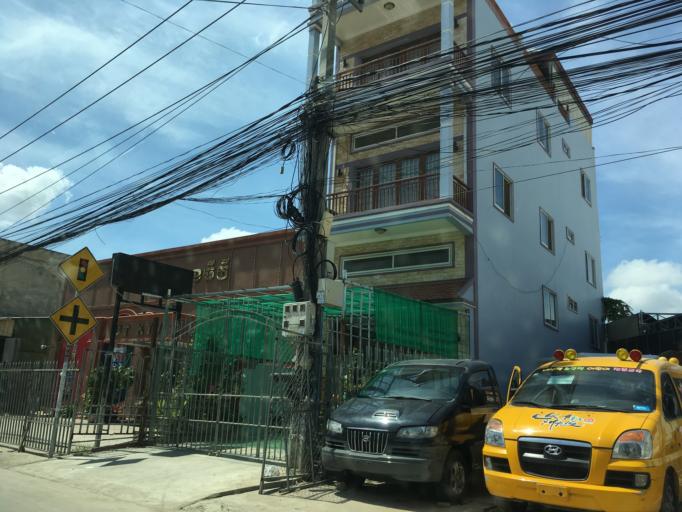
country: KH
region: Phnom Penh
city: Phnom Penh
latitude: 11.5505
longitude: 104.8606
